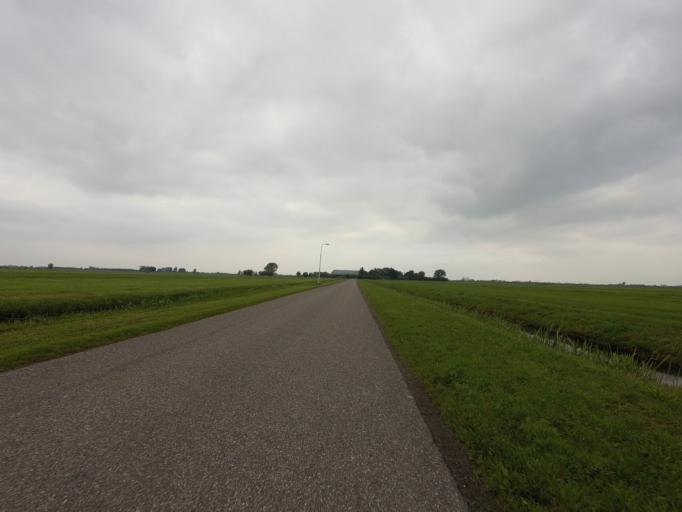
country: NL
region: South Holland
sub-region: Molenwaard
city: Liesveld
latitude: 51.8887
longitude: 4.7915
